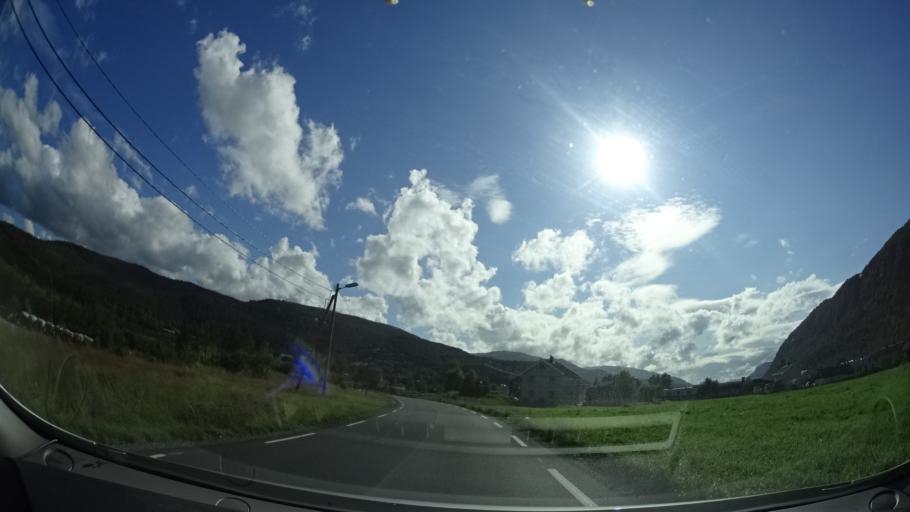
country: NO
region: Sor-Trondelag
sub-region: Hemne
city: Kyrksaeterora
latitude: 63.2055
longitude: 8.9908
